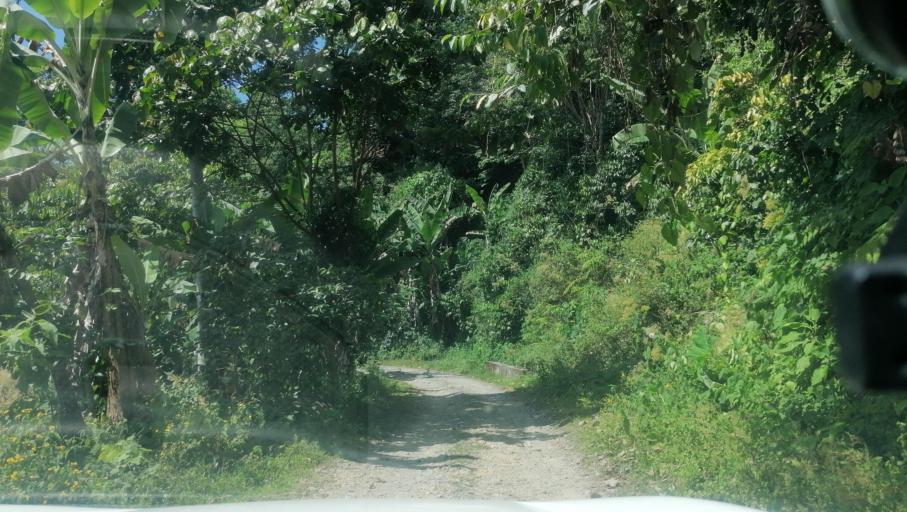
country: MX
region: Chiapas
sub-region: Union Juarez
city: Santo Domingo
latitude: 15.0761
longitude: -92.1301
